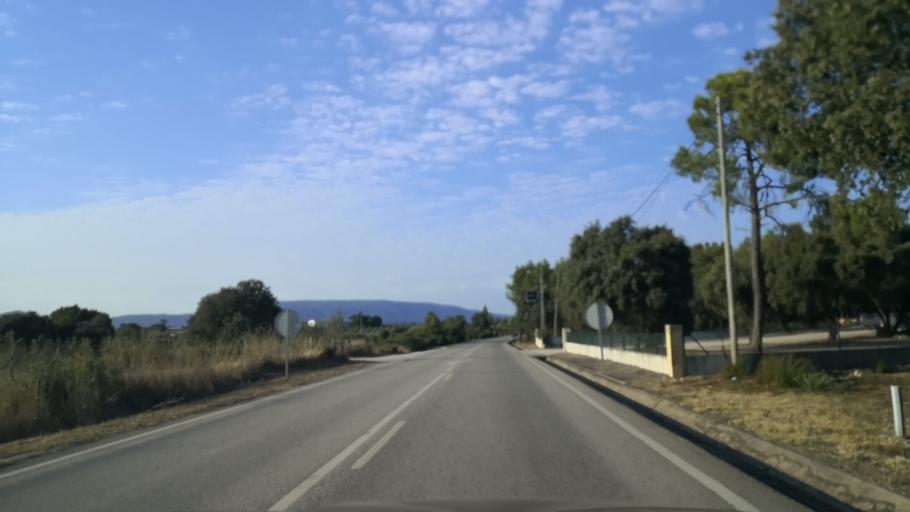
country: PT
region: Santarem
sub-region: Alcanena
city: Alcanena
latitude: 39.4249
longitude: -8.6346
